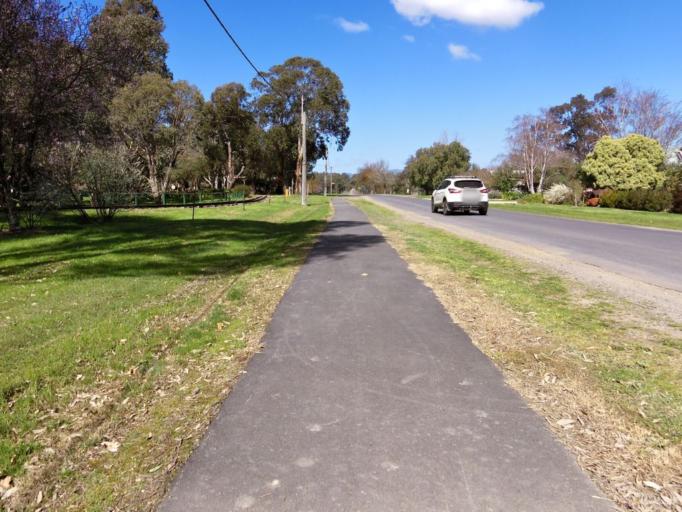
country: AU
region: Victoria
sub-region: Murrindindi
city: Alexandra
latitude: -37.1848
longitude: 145.7136
